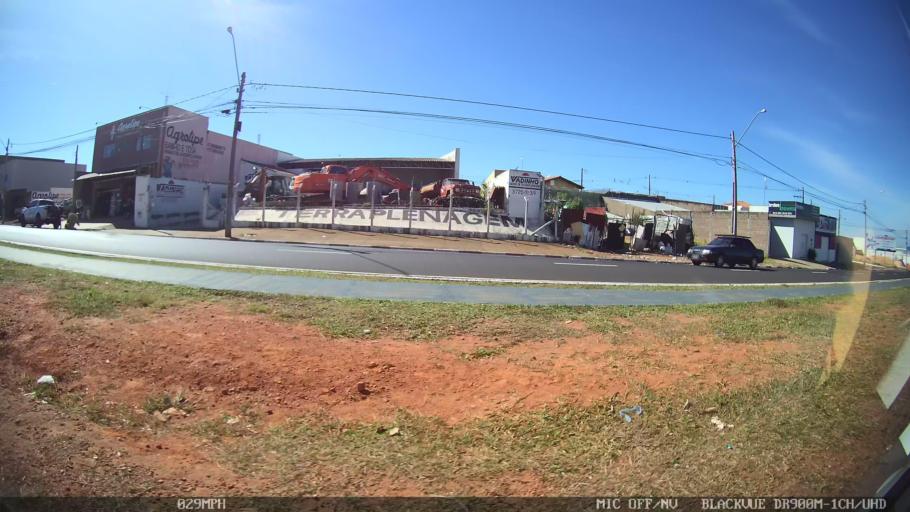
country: BR
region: Sao Paulo
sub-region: Franca
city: Franca
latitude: -20.5426
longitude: -47.3596
